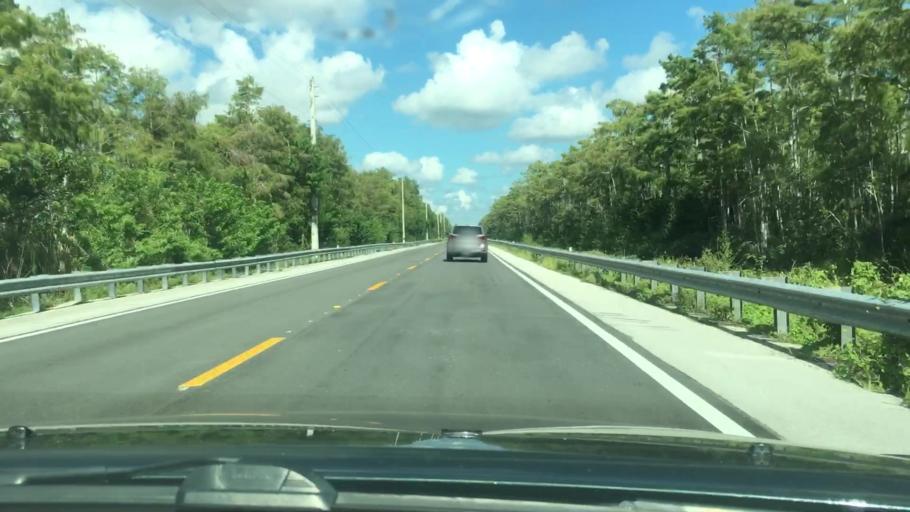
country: US
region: Florida
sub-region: Miami-Dade County
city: Kendall West
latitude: 25.7994
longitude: -80.8668
